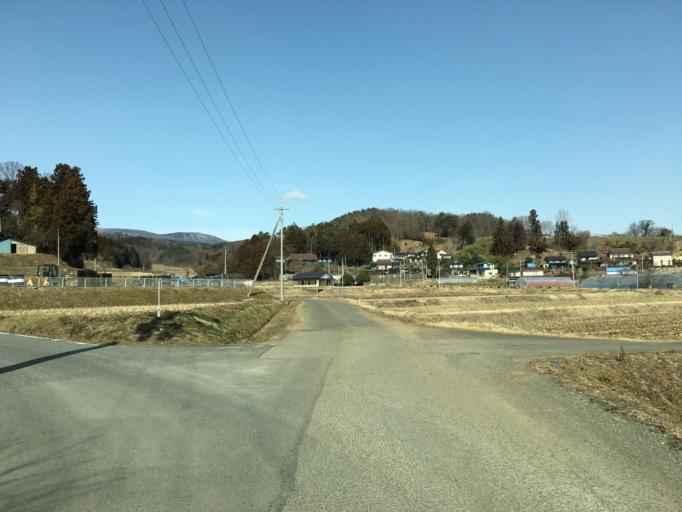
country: JP
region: Fukushima
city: Nihommatsu
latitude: 37.5766
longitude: 140.3805
